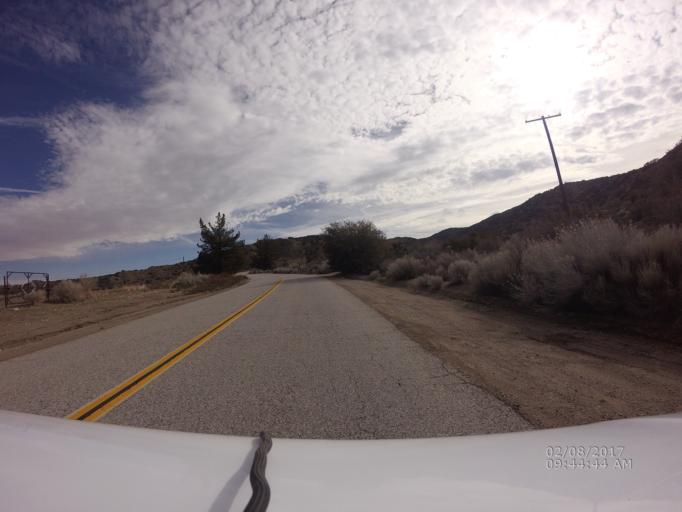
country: US
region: California
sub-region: Los Angeles County
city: Littlerock
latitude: 34.4325
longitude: -117.8313
